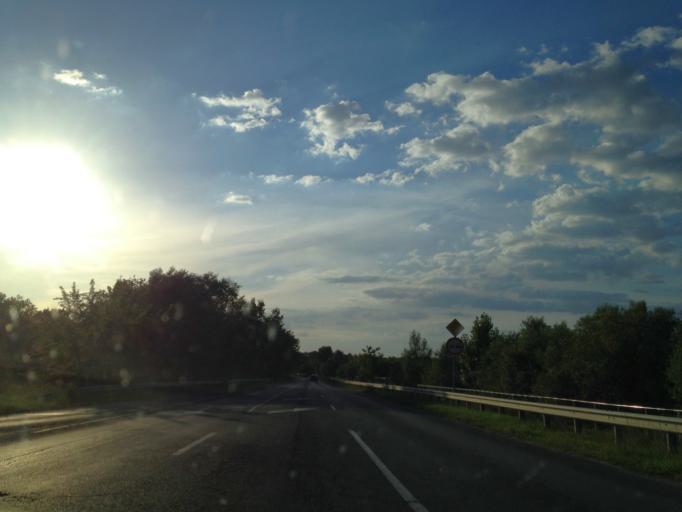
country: HU
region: Gyor-Moson-Sopron
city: Abda
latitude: 47.6842
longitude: 17.5688
